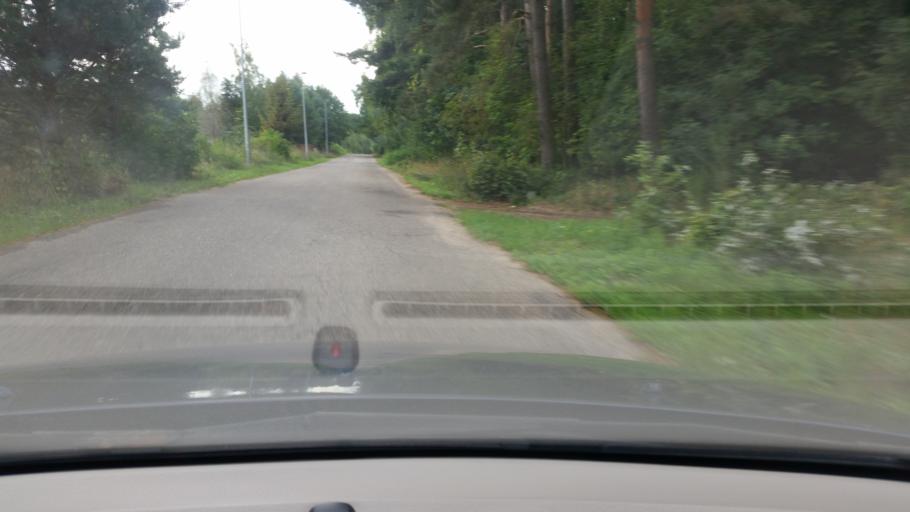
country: PL
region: Pomeranian Voivodeship
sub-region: Powiat wejherowski
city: Choczewo
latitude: 54.7651
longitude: 17.7931
